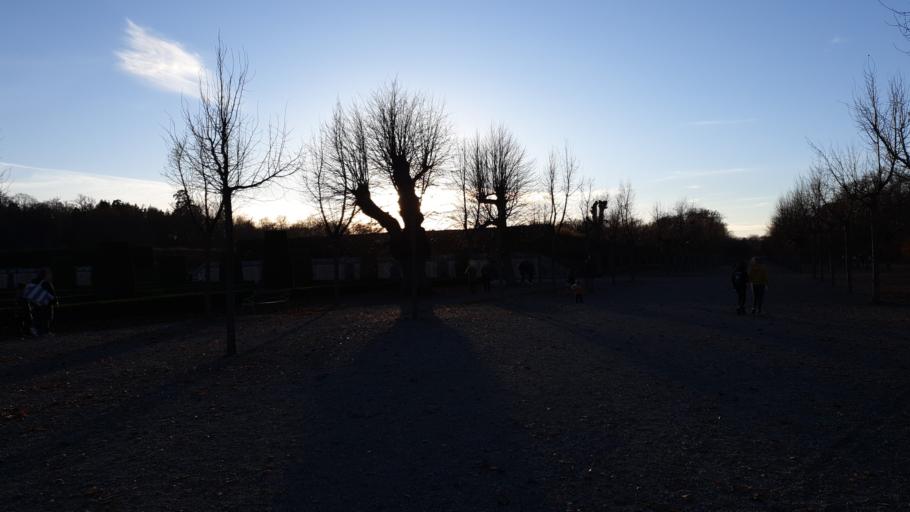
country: SE
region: Stockholm
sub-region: Stockholms Kommun
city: Bromma
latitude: 59.3215
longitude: 17.8820
